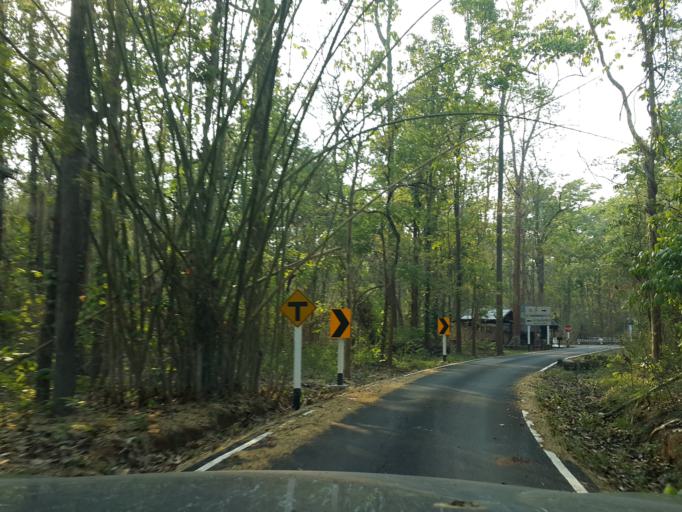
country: TH
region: Lamphun
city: Li
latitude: 17.6459
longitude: 98.8766
